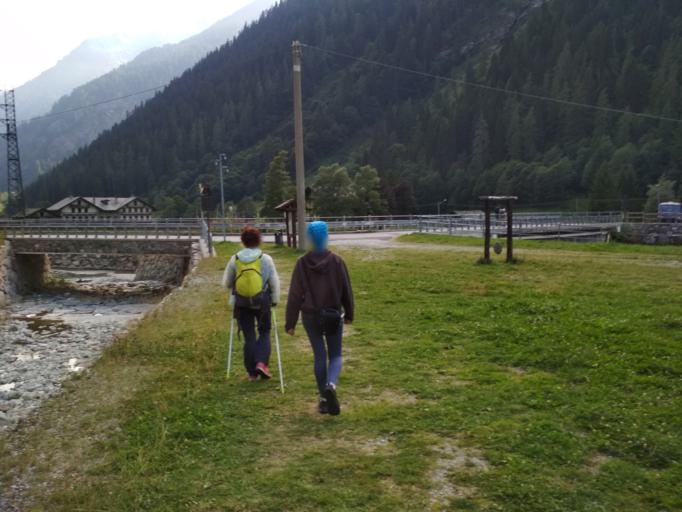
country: IT
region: Aosta Valley
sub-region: Valle d'Aosta
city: Gressoney-Saint-Jean
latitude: 45.7939
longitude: 7.8240
